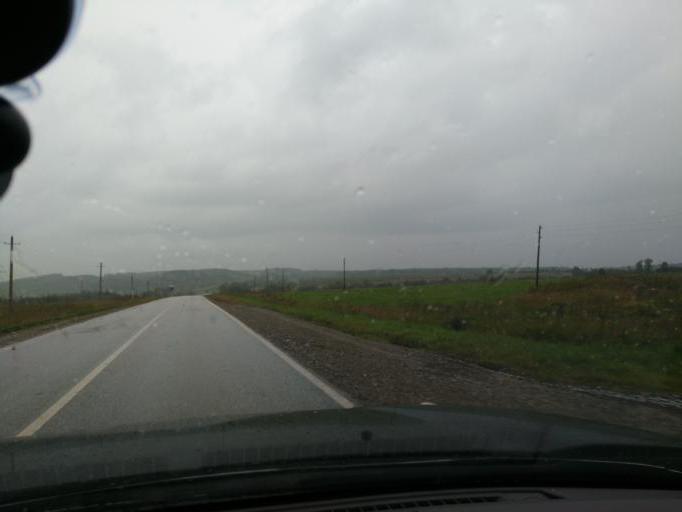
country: RU
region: Perm
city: Barda
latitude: 57.1014
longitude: 55.5287
